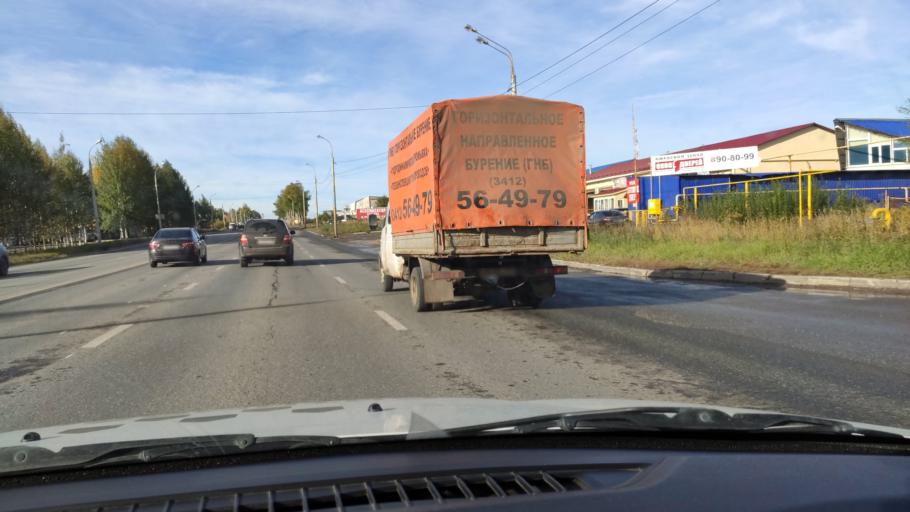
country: RU
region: Udmurtiya
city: Khokhryaki
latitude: 56.9035
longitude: 53.3348
